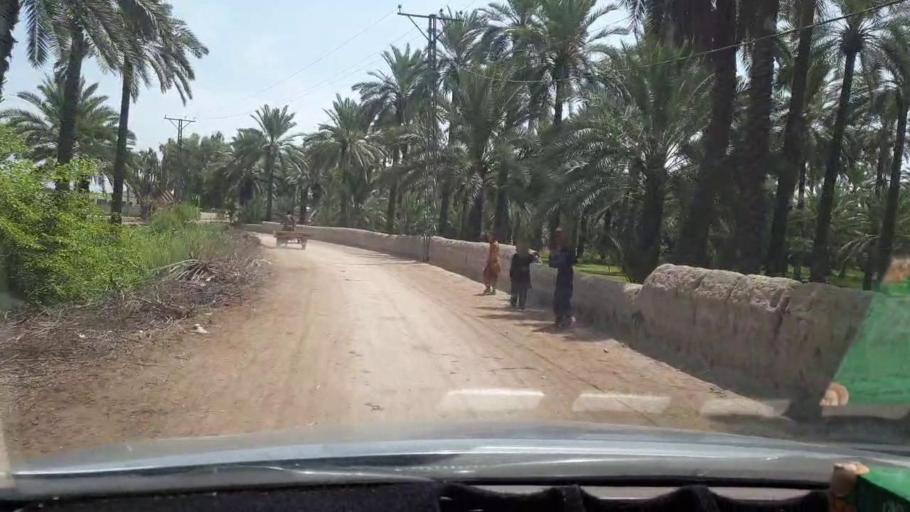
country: PK
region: Sindh
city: Khairpur
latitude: 27.4862
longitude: 68.7694
